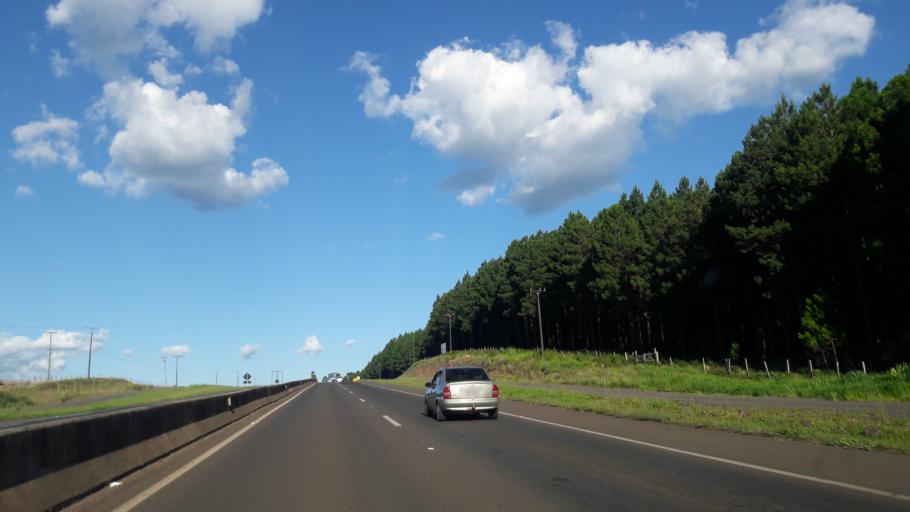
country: BR
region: Parana
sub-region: Guarapuava
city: Guarapuava
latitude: -25.3440
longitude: -51.4397
